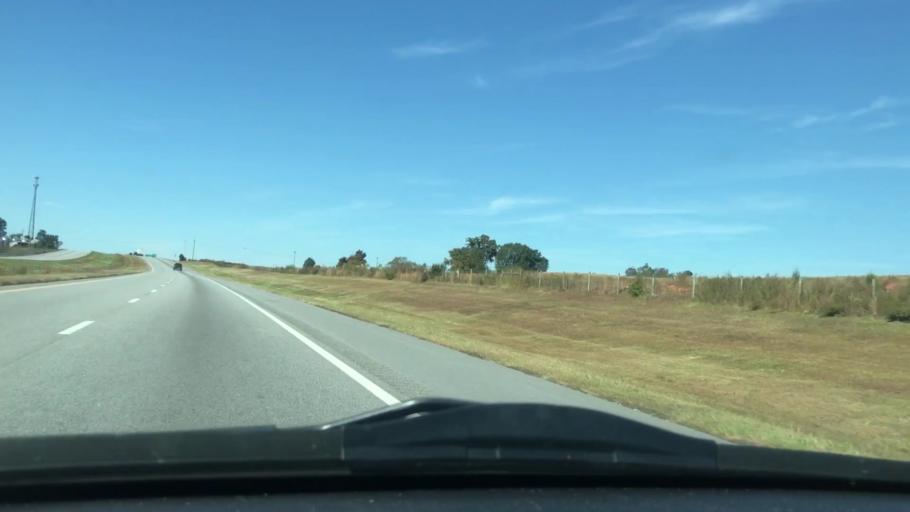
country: US
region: North Carolina
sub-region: Randolph County
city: Archdale
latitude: 35.8661
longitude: -79.8915
